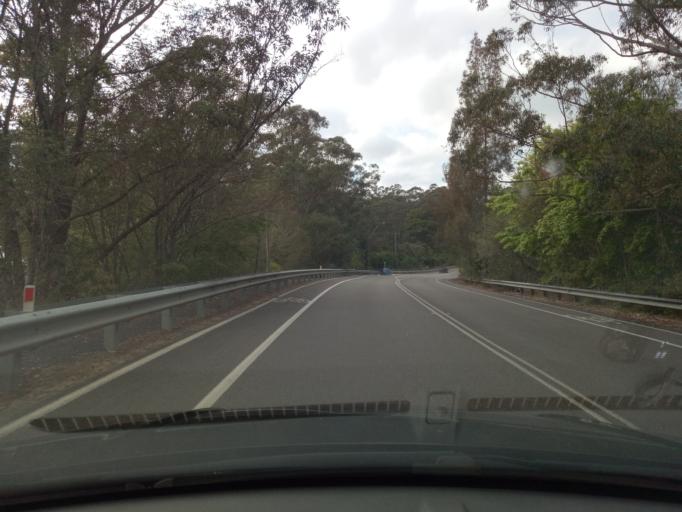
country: AU
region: New South Wales
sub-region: Gosford Shire
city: Erina
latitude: -33.4304
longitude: 151.3743
